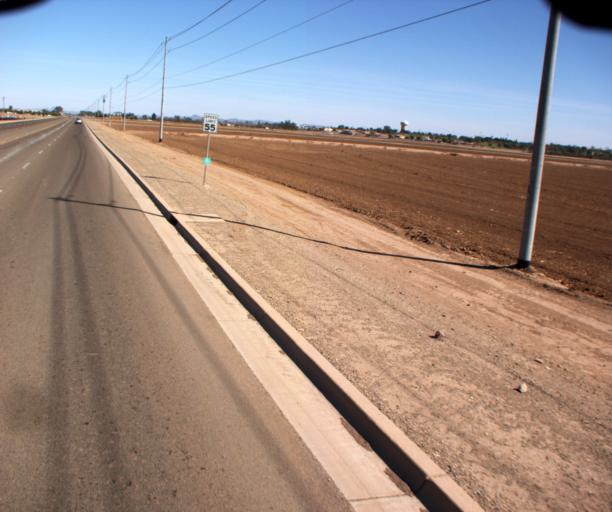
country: US
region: Arizona
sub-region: Yuma County
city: Somerton
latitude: 32.6481
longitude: -114.6500
